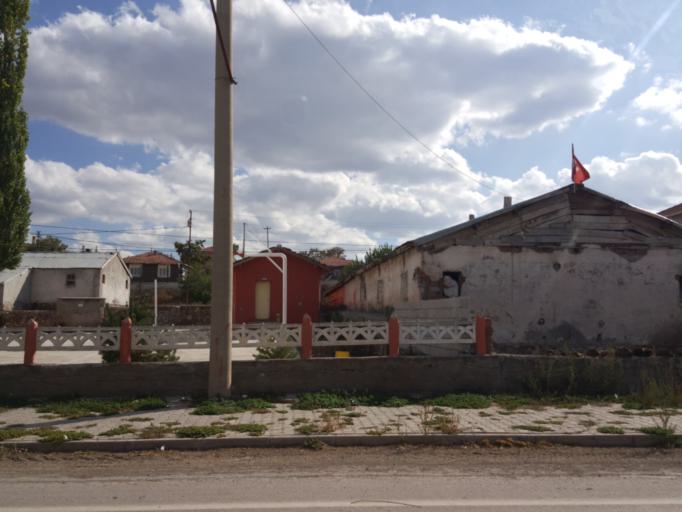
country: TR
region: Tokat
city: Yesilyurt
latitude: 40.0079
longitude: 36.2096
